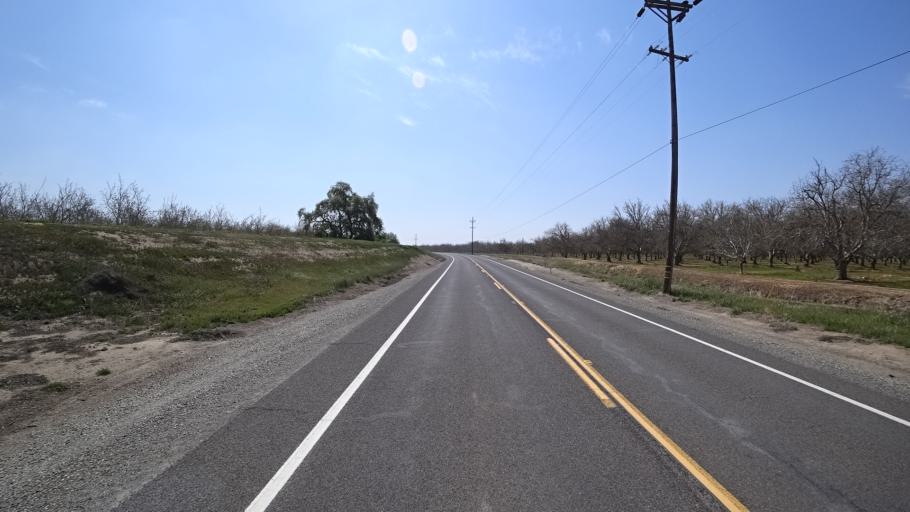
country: US
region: California
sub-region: Glenn County
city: Willows
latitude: 39.4920
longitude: -122.0205
